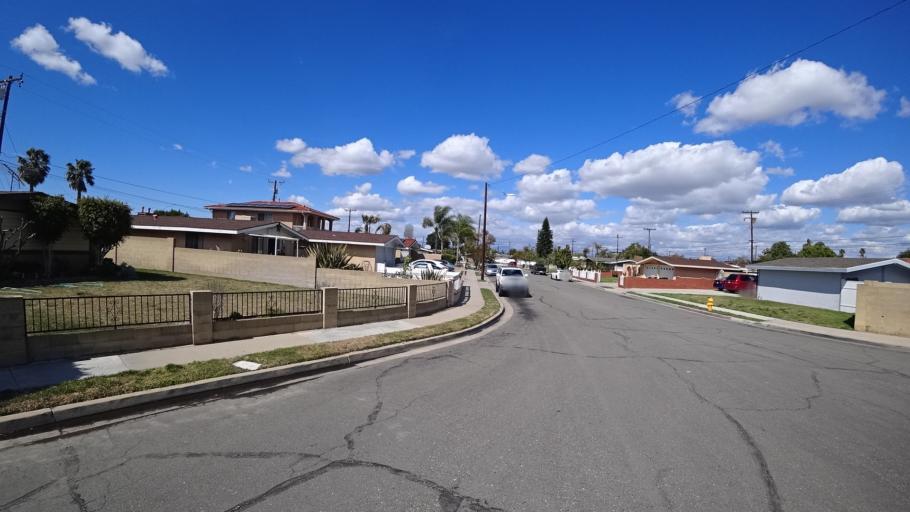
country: US
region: California
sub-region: Orange County
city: Anaheim
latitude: 33.8340
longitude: -117.8918
